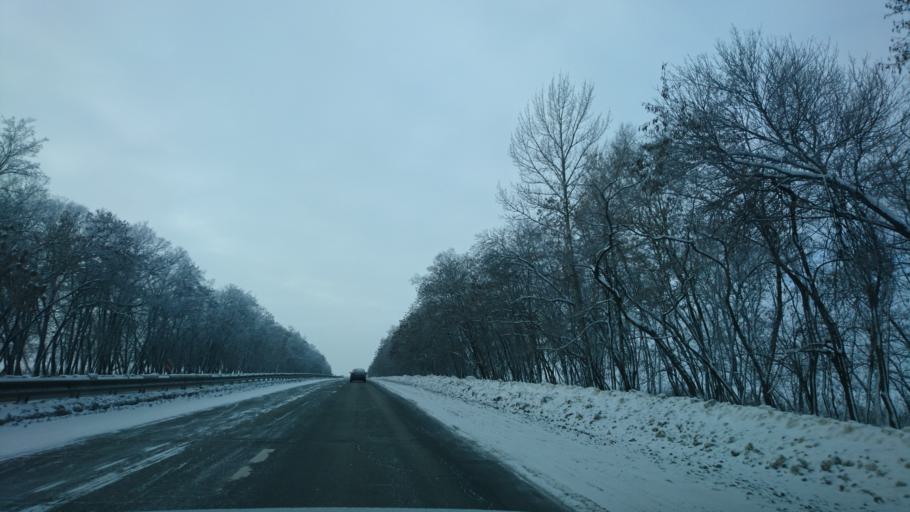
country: RU
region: Belgorod
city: Mayskiy
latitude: 50.4919
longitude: 36.4211
